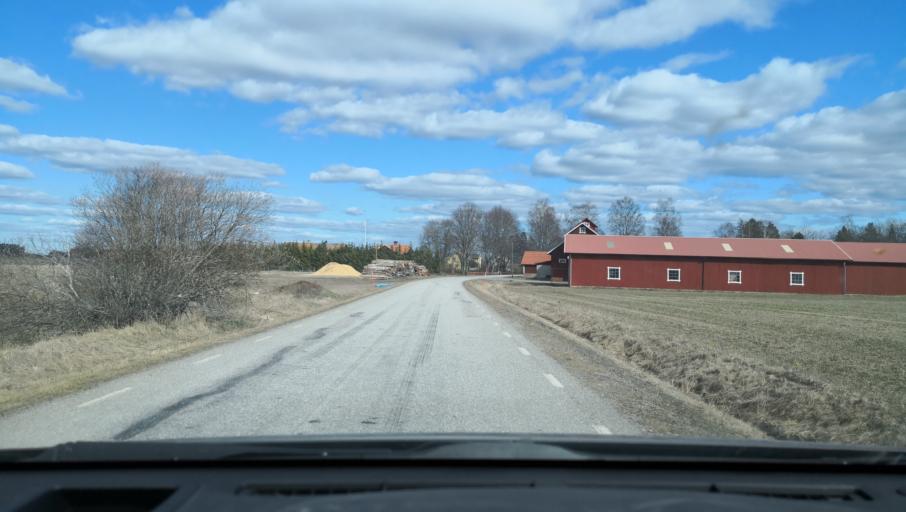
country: SE
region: Vaestmanland
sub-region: Sala Kommun
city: Sala
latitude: 59.8591
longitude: 16.6175
